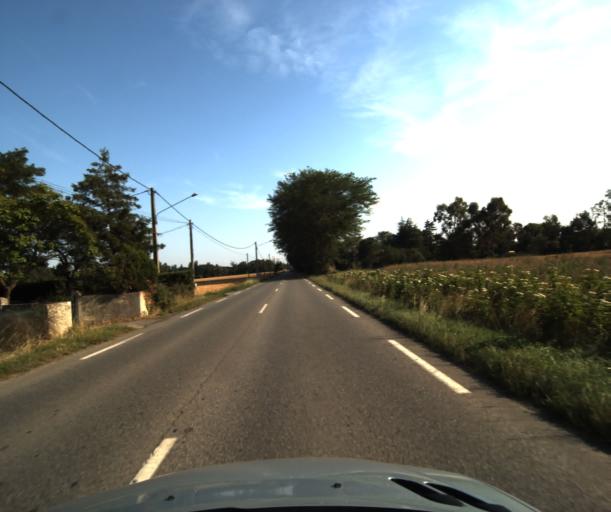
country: FR
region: Midi-Pyrenees
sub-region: Departement de la Haute-Garonne
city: Labarthe-sur-Leze
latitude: 43.4731
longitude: 1.3978
